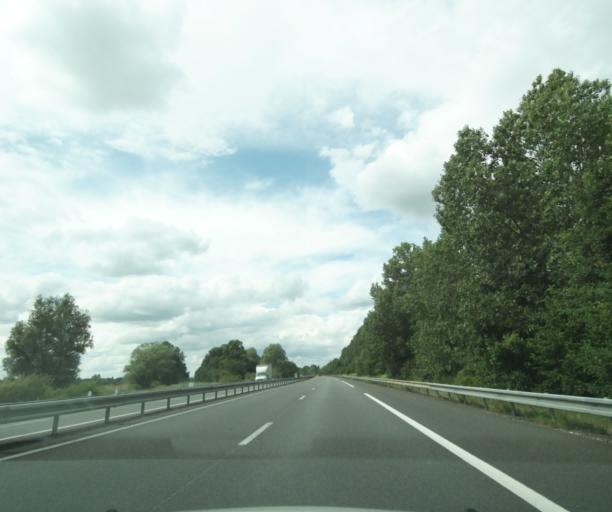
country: FR
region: Centre
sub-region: Departement du Cher
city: Foecy
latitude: 47.1691
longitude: 2.1810
